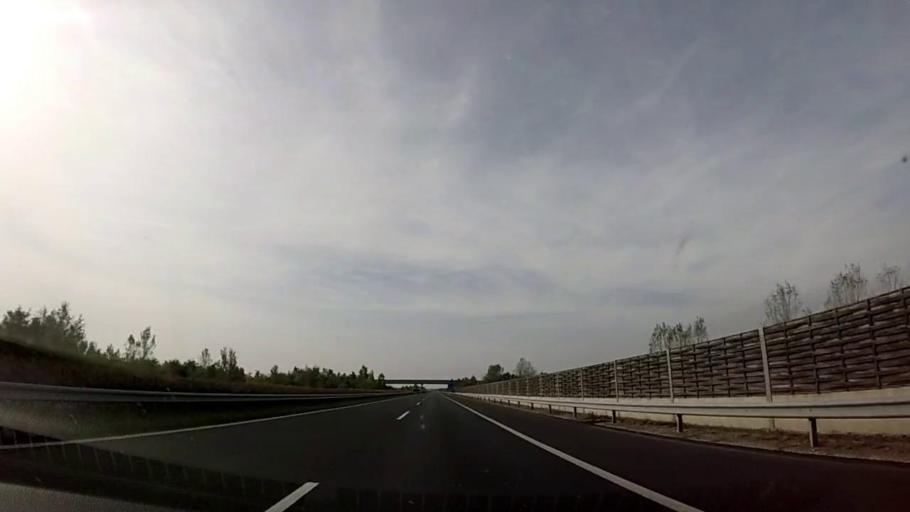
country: HU
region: Somogy
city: Fonyod
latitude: 46.7353
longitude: 17.5991
